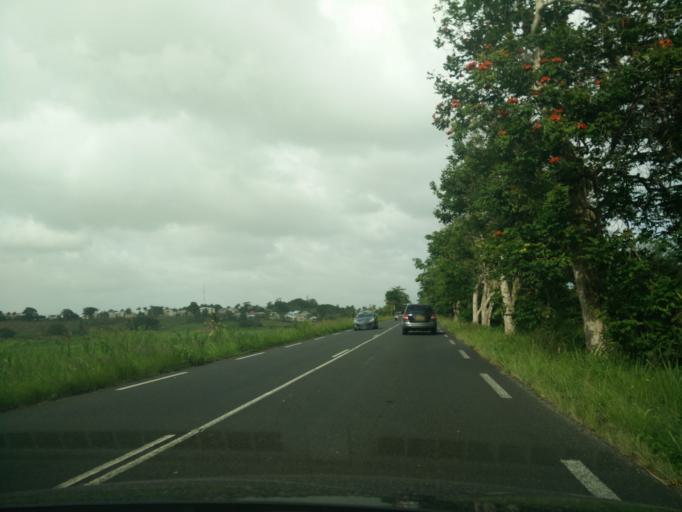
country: GP
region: Guadeloupe
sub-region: Guadeloupe
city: Petit-Bourg
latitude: 16.2171
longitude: -61.6087
